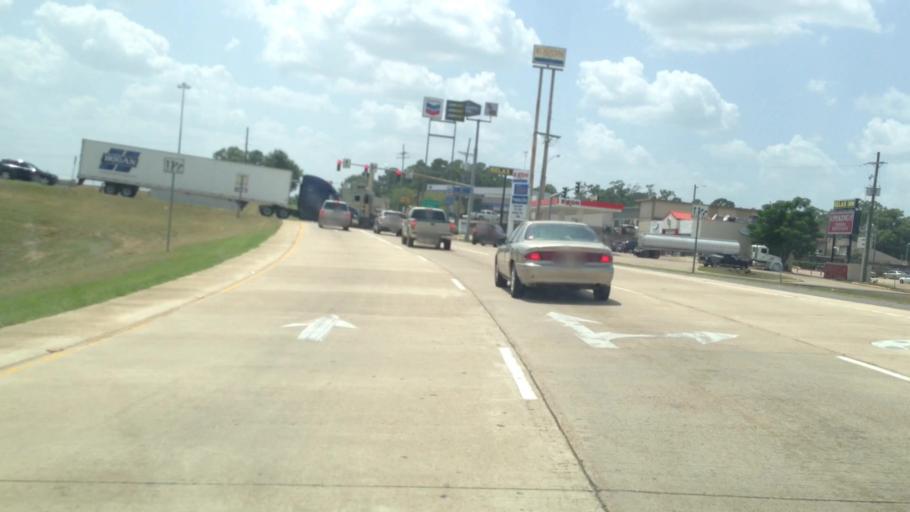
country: US
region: Louisiana
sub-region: Lincoln Parish
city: Ruston
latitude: 32.5410
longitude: -92.6371
